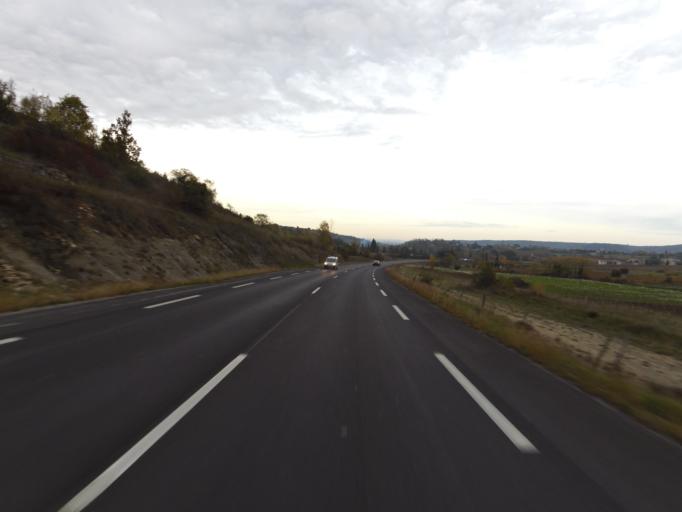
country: FR
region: Rhone-Alpes
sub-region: Departement de l'Ardeche
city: Joyeuse
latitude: 44.4743
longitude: 4.2393
